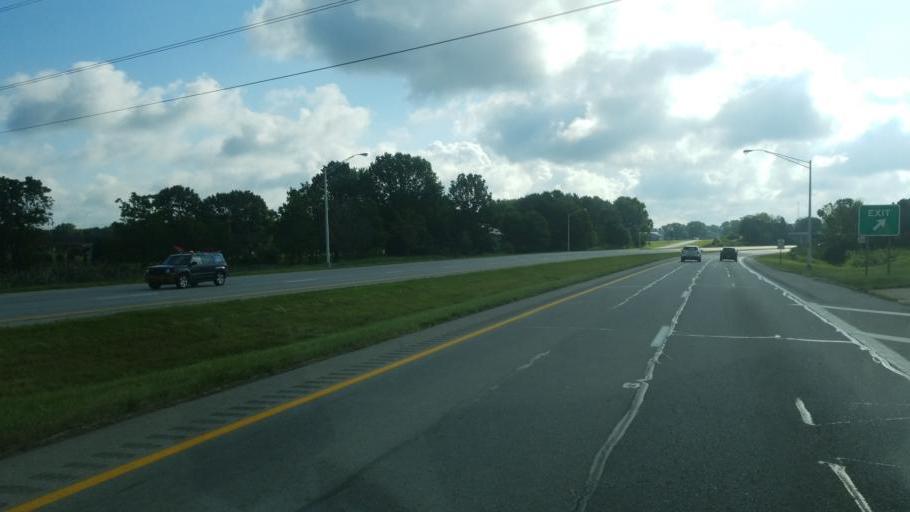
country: US
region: Ohio
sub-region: Wayne County
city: Dalton
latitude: 40.7979
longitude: -81.6569
